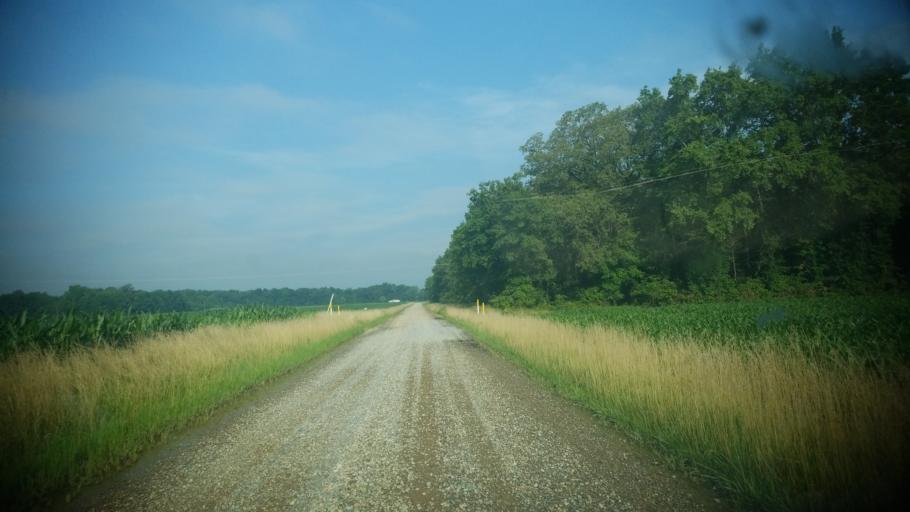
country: US
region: Illinois
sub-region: Clay County
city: Flora
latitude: 38.6020
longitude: -88.3579
